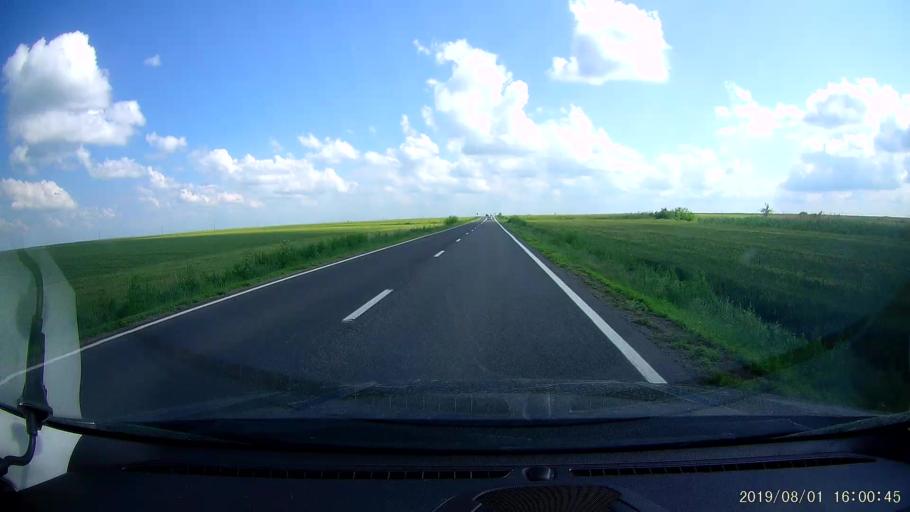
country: RO
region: Ialomita
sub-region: Comuna Ciulnita
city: Ciulnita
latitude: 44.5216
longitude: 27.3894
